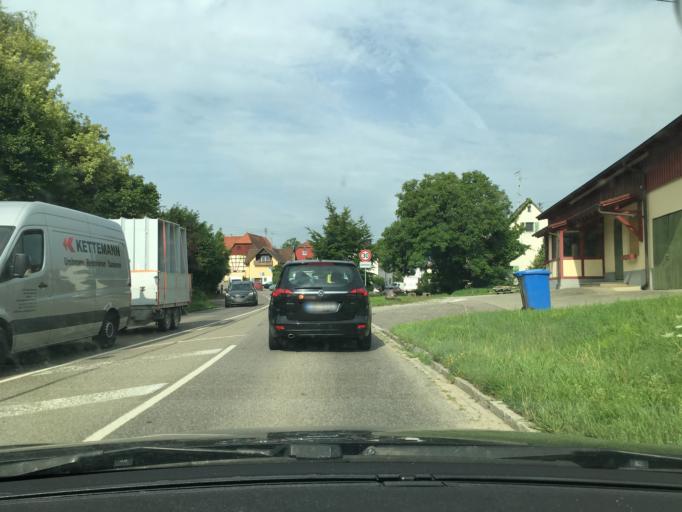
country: DE
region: Baden-Wuerttemberg
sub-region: Tuebingen Region
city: Stetten
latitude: 47.6927
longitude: 9.3014
